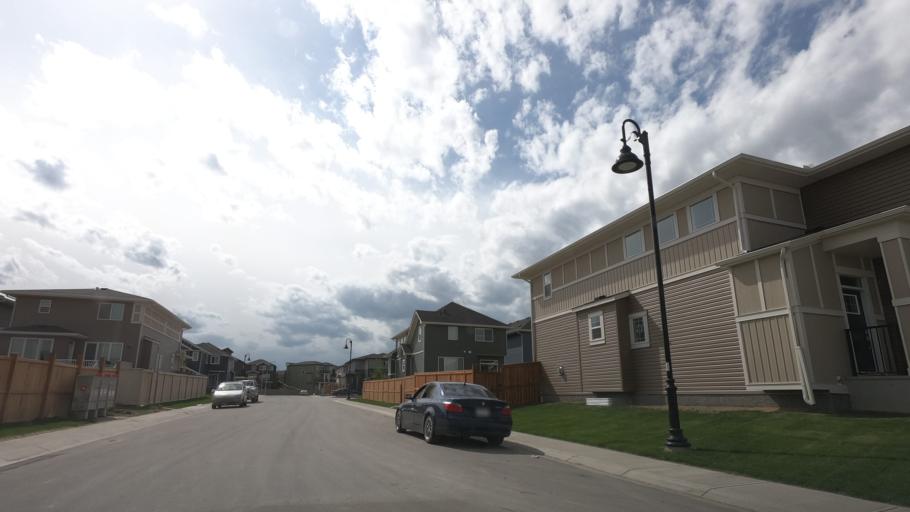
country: CA
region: Alberta
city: Airdrie
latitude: 51.2761
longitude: -114.0416
